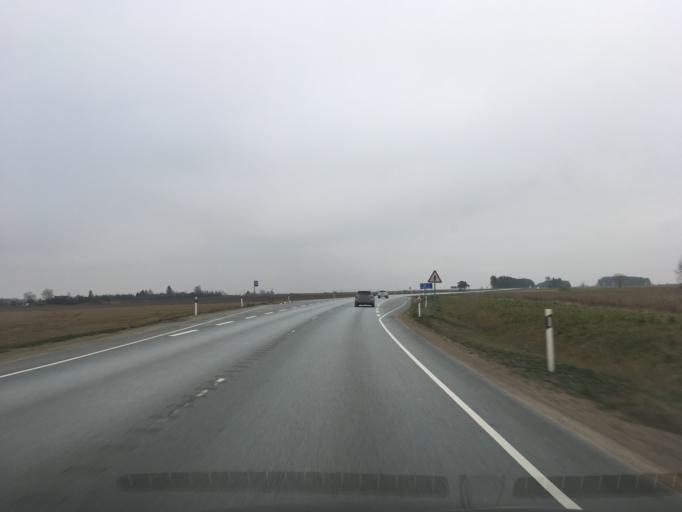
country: EE
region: Ida-Virumaa
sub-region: Puessi linn
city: Pussi
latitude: 59.4117
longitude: 27.0421
